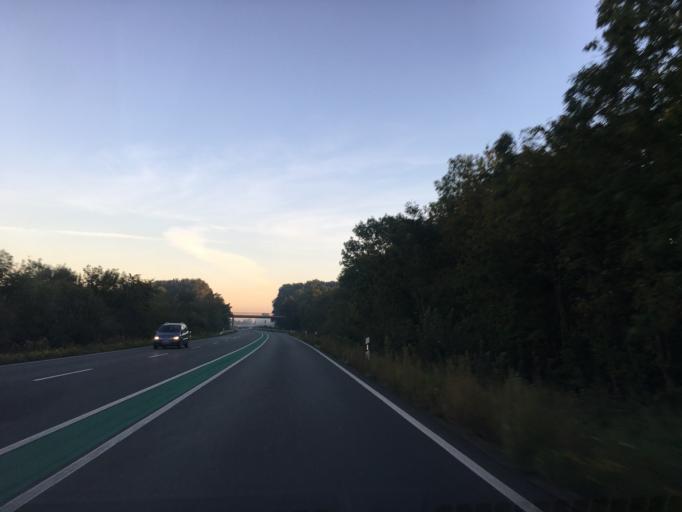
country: DE
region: North Rhine-Westphalia
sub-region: Regierungsbezirk Munster
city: Altenberge
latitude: 52.0885
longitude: 7.4154
